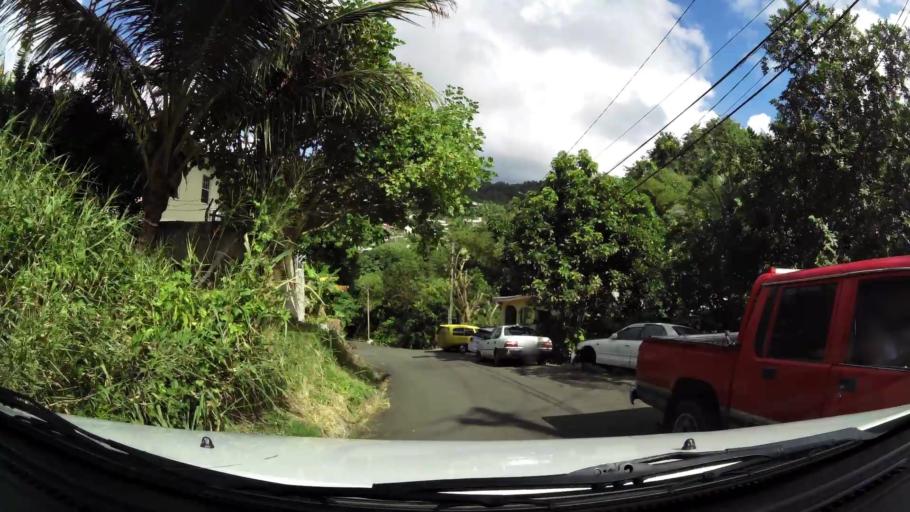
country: LC
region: Castries Quarter
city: Bisee
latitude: 14.0012
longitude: -60.9781
